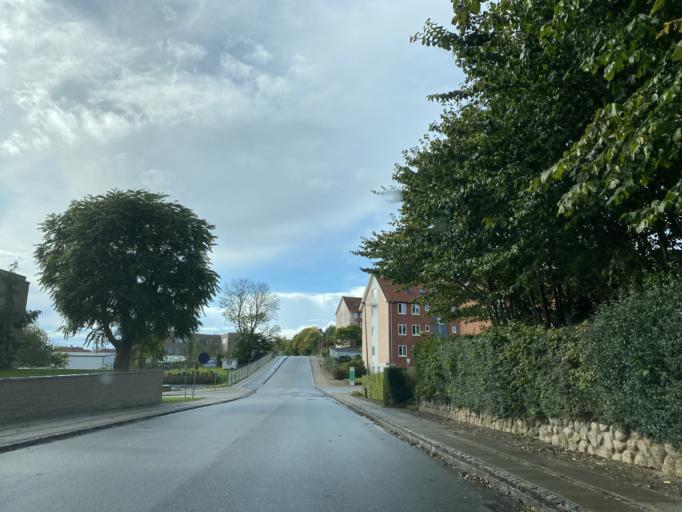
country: DK
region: South Denmark
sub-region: Haderslev Kommune
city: Haderslev
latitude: 55.2568
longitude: 9.4861
